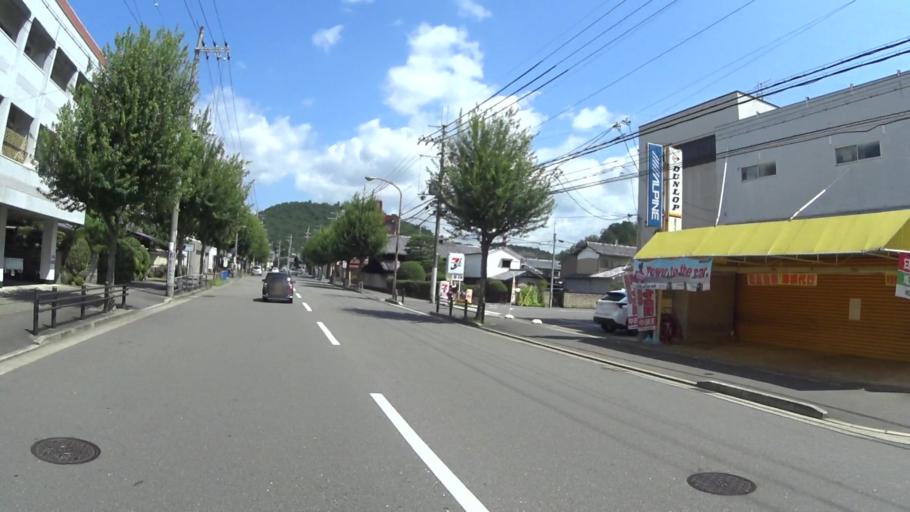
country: JP
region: Kyoto
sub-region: Kyoto-shi
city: Kamigyo-ku
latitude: 35.0543
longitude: 135.7671
